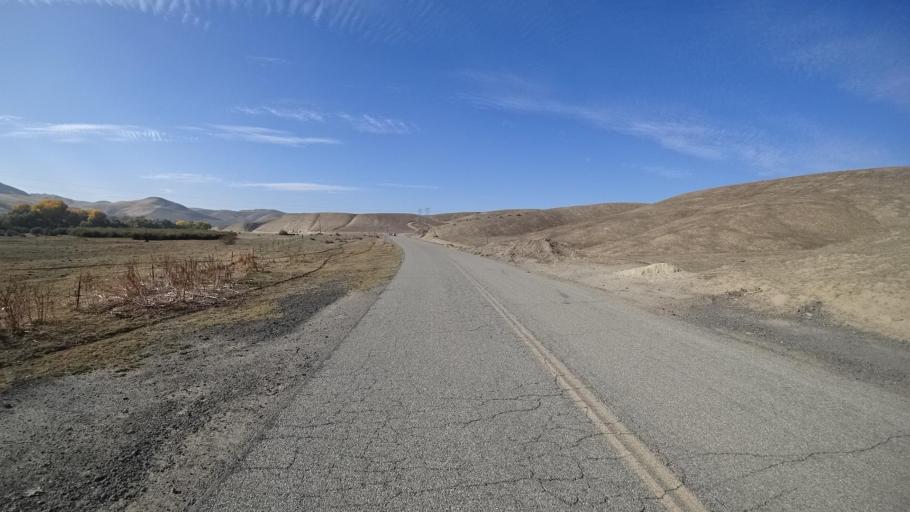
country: US
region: California
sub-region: Kern County
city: Oildale
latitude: 35.5179
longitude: -118.9154
